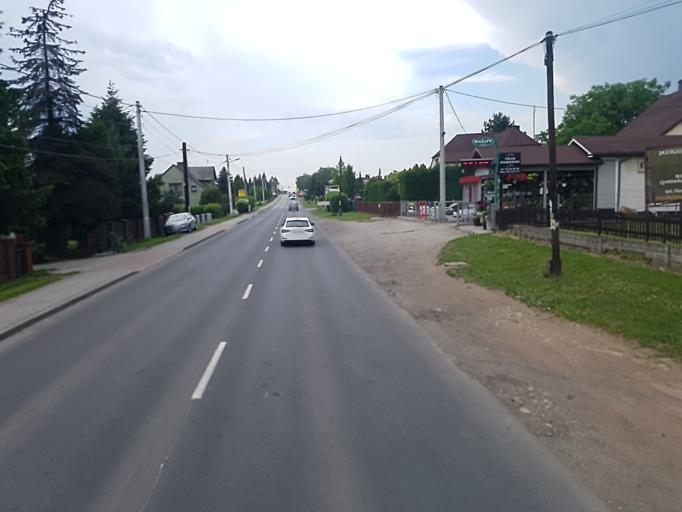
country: PL
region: Silesian Voivodeship
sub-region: Powiat wodzislawski
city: Wodzislaw Slaski
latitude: 49.9885
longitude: 18.4995
